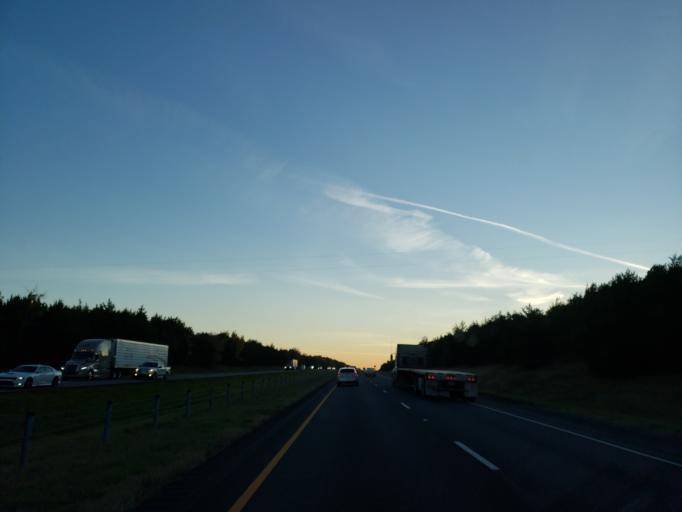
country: US
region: Alabama
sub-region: Sumter County
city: Livingston
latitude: 32.6708
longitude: -88.1726
